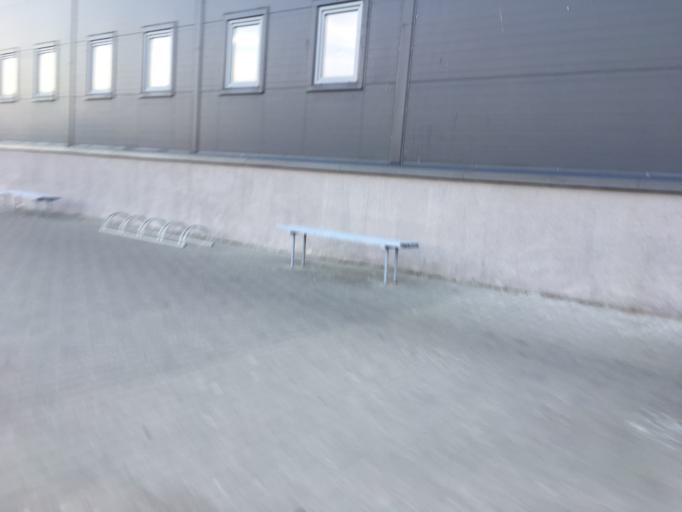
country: BY
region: Grodnenskaya
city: Hrodna
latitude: 53.7086
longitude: 23.8602
